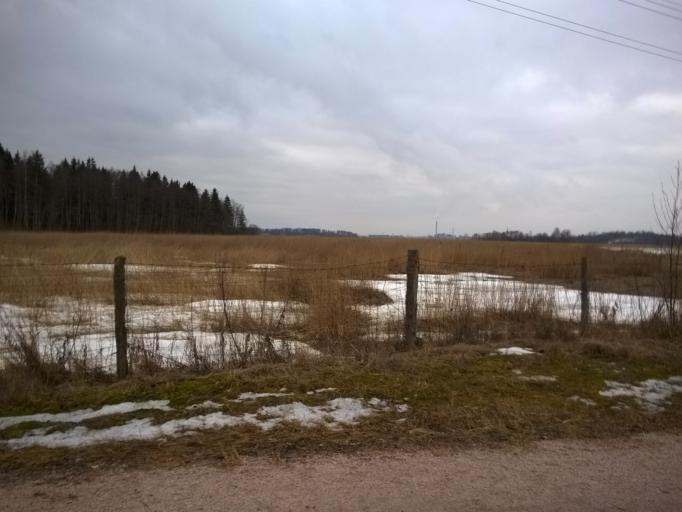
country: FI
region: Uusimaa
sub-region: Helsinki
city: Vantaa
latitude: 60.2144
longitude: 25.0205
